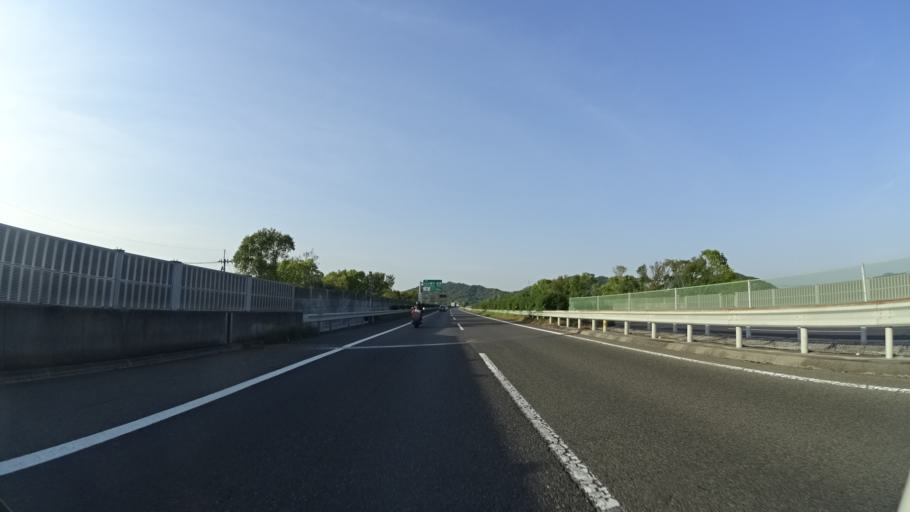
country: JP
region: Kagawa
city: Kan'onjicho
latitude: 34.1415
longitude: 133.7118
